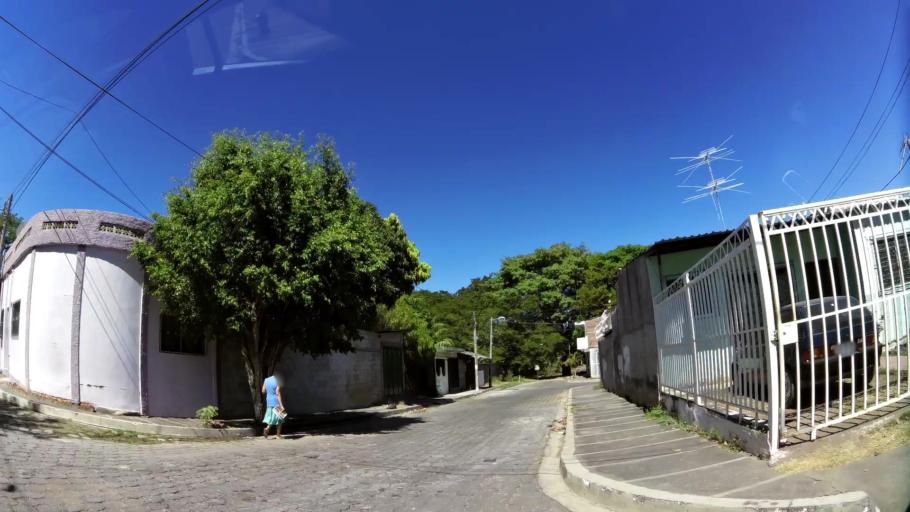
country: SV
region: San Miguel
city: San Miguel
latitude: 13.4883
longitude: -88.1738
